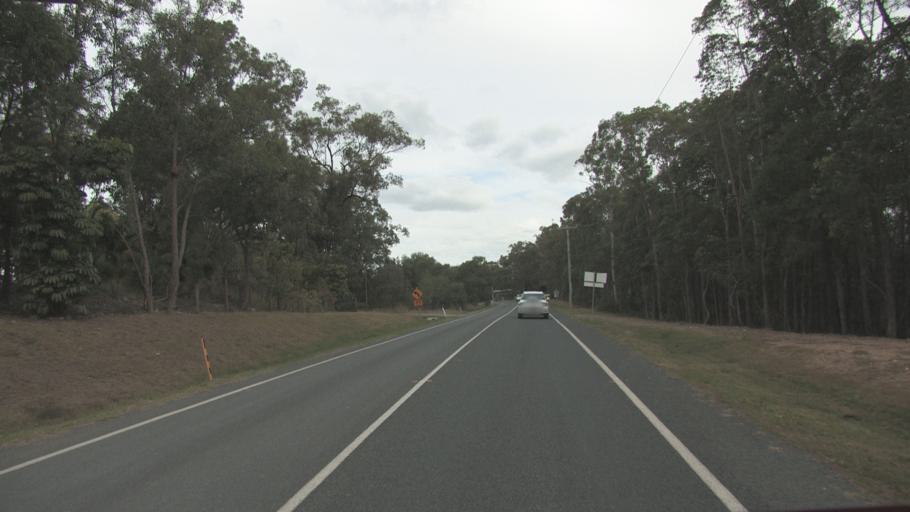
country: AU
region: Queensland
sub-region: Logan
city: Waterford West
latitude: -27.7218
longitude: 153.1597
